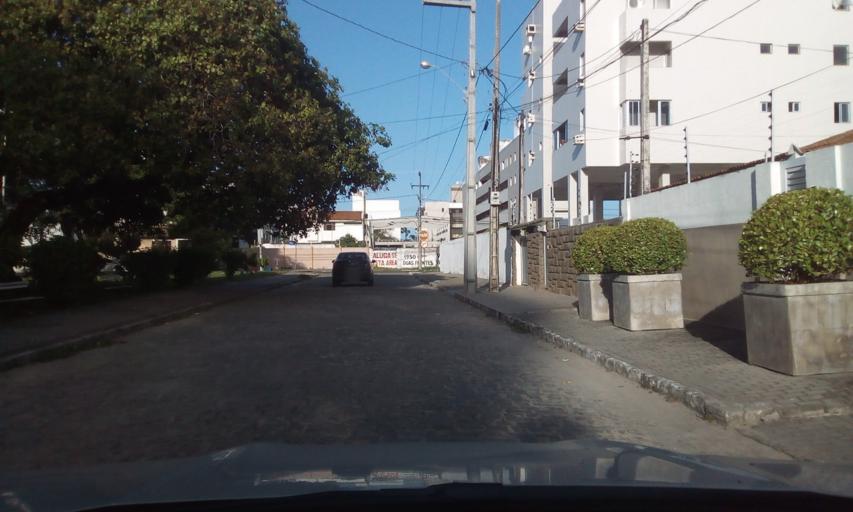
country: BR
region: Paraiba
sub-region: Joao Pessoa
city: Joao Pessoa
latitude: -7.0926
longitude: -34.8363
